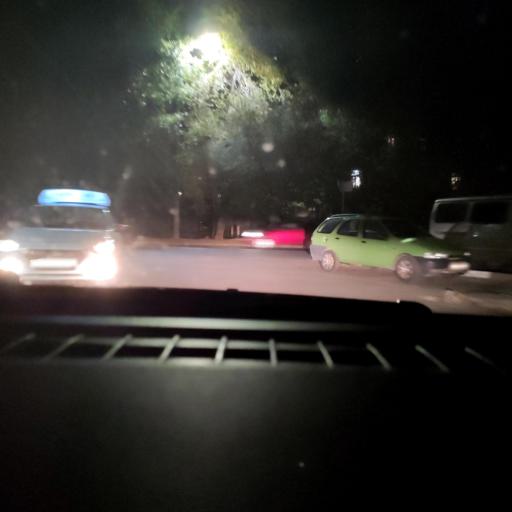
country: RU
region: Voronezj
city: Voronezh
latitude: 51.6832
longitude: 39.1936
